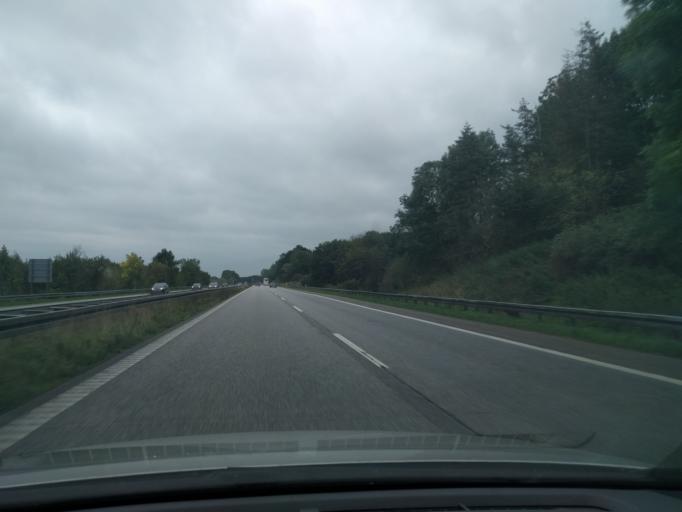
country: DK
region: Zealand
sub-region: Slagelse Kommune
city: Slagelse
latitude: 55.4013
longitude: 11.3893
